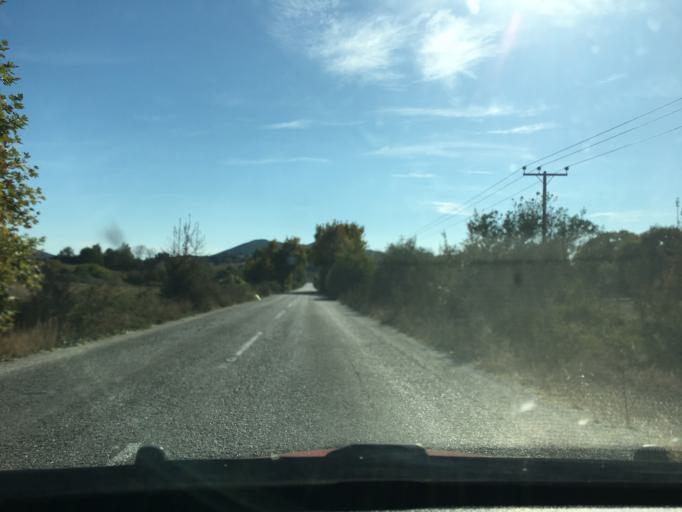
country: GR
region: Central Macedonia
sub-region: Nomos Chalkidikis
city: Megali Panagia
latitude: 40.3741
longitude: 23.6948
